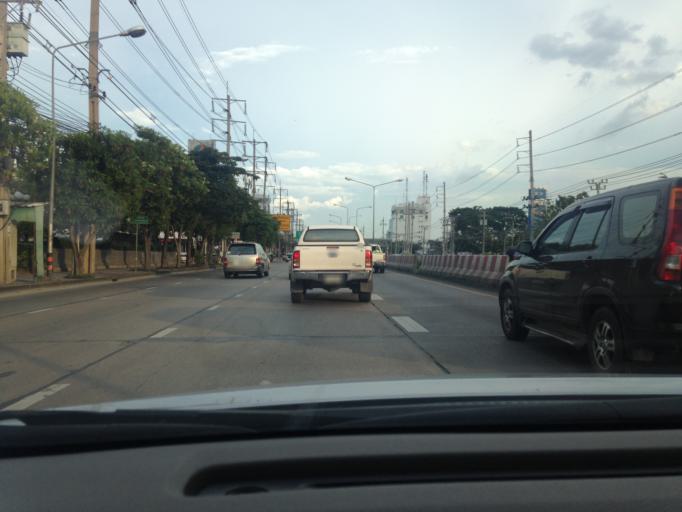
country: TH
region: Bangkok
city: Lak Si
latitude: 13.8878
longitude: 100.5753
